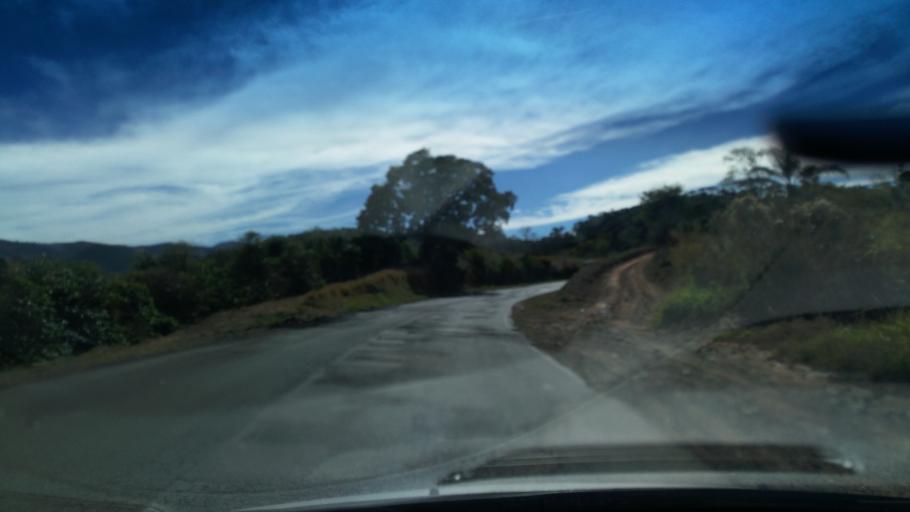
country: BR
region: Minas Gerais
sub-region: Andradas
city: Andradas
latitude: -22.0550
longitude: -46.3654
